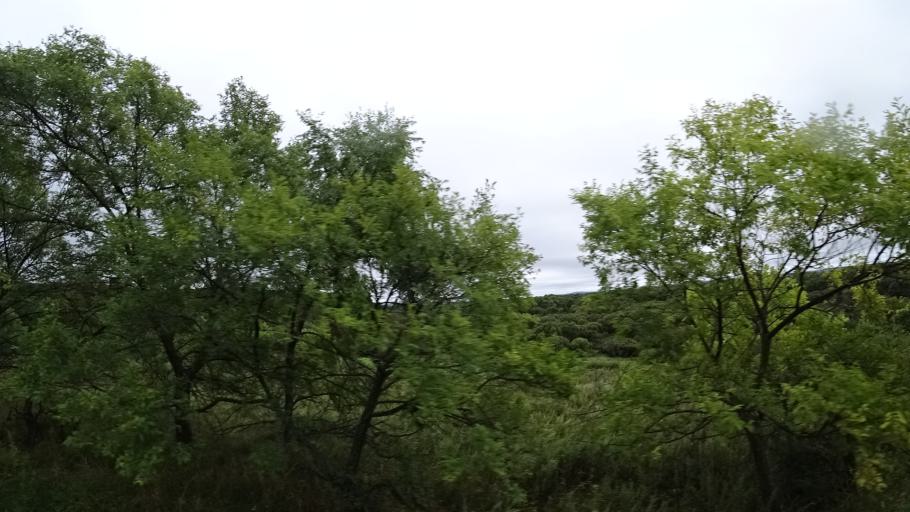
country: RU
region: Primorskiy
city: Monastyrishche
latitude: 44.2588
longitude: 132.4101
